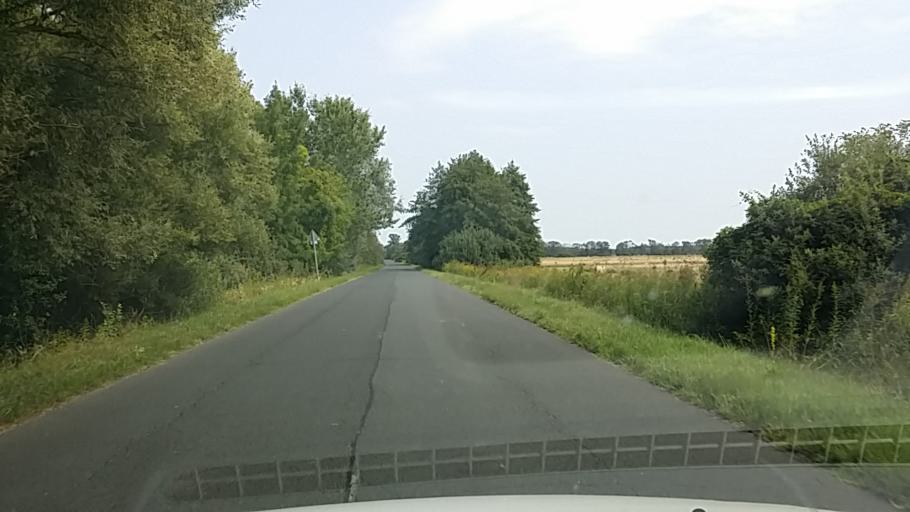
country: HU
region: Gyor-Moson-Sopron
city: Lebeny
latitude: 47.7365
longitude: 17.3358
